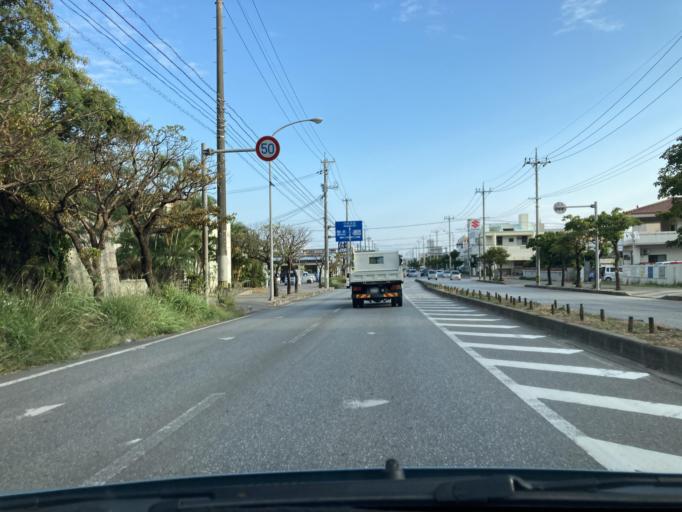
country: JP
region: Okinawa
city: Gushikawa
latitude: 26.3413
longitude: 127.8438
